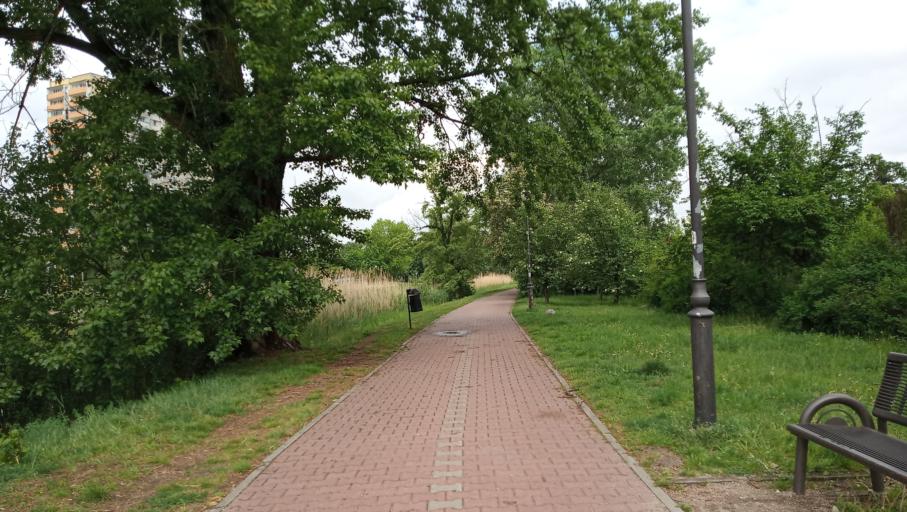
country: PL
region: Masovian Voivodeship
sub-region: Warszawa
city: Zoliborz
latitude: 52.2838
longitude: 20.9811
